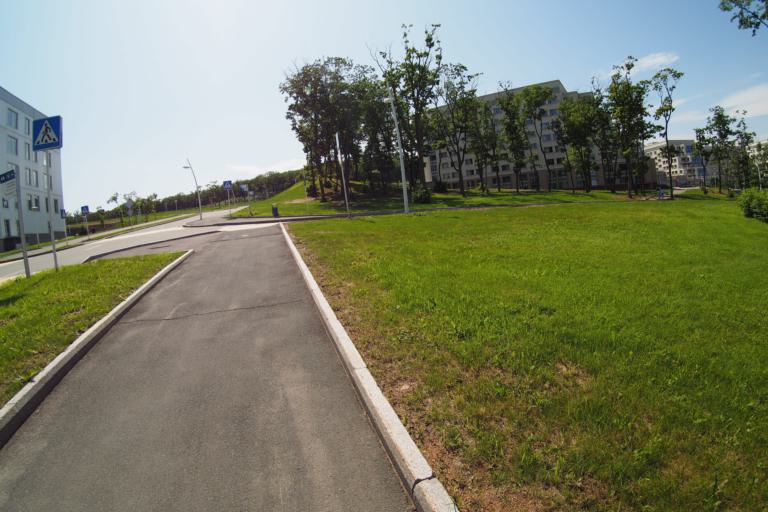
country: RU
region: Primorskiy
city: Russkiy
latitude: 43.0269
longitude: 131.8883
